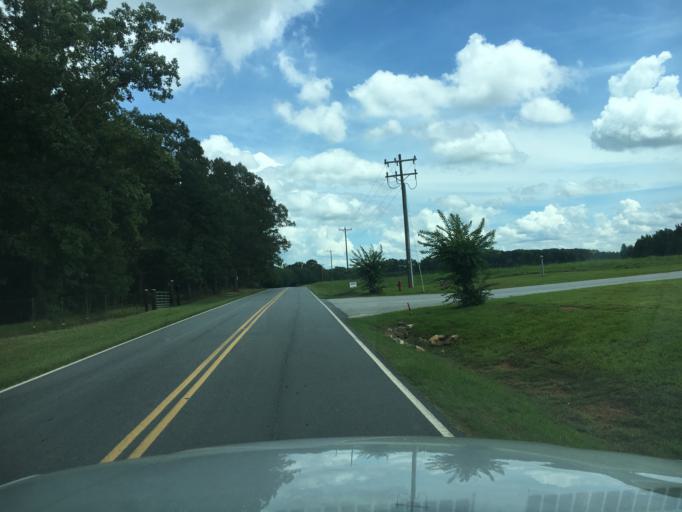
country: US
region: South Carolina
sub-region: Anderson County
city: Belton
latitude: 34.5436
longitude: -82.4526
